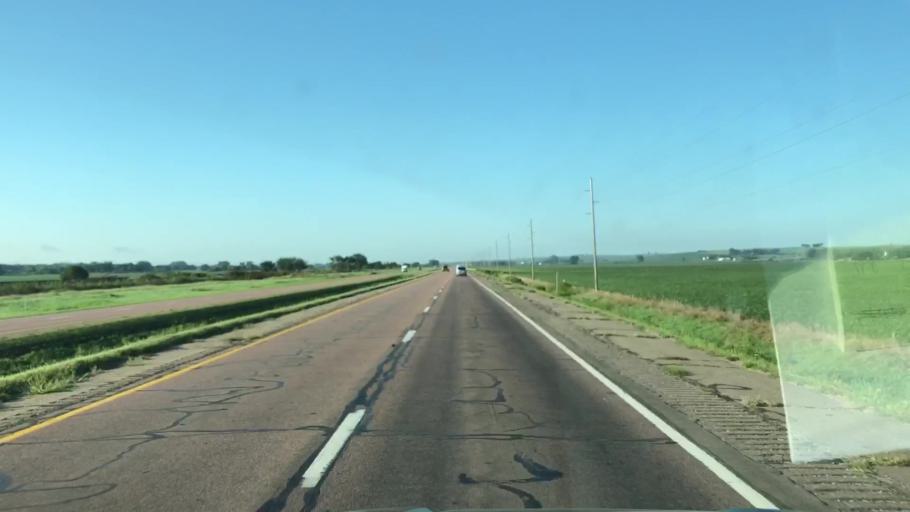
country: US
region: Iowa
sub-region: Plymouth County
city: Le Mars
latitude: 42.7026
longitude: -96.2568
